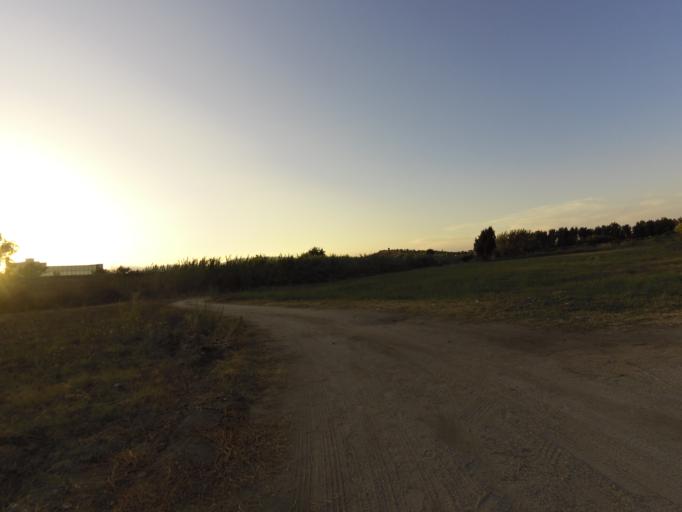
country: IT
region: Calabria
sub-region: Provincia di Reggio Calabria
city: Monasterace Marina
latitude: 38.4497
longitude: 16.5803
